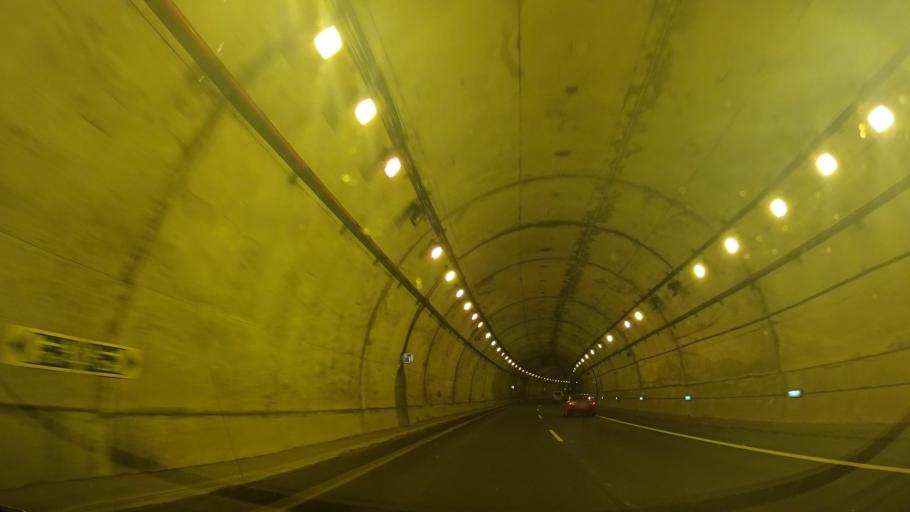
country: ES
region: Asturias
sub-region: Province of Asturias
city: Arriba
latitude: 43.5068
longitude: -5.5799
